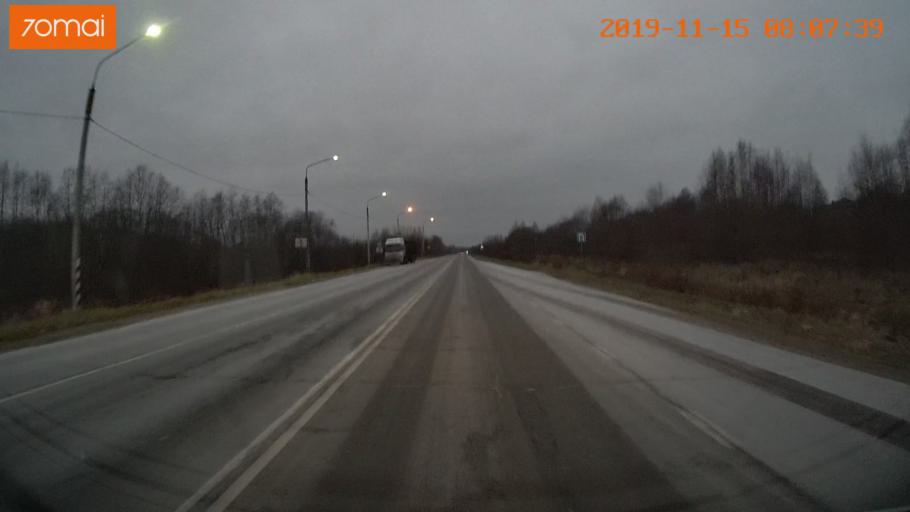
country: RU
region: Vologda
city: Cherepovets
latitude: 59.0275
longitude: 38.0111
